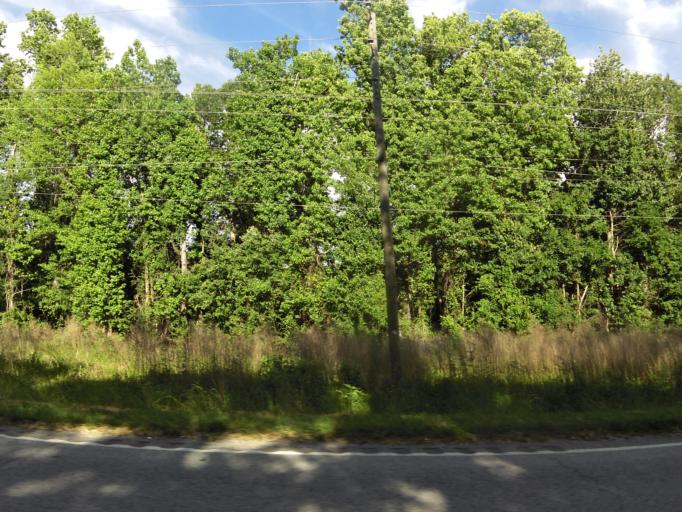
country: US
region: South Carolina
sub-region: Allendale County
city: Fairfax
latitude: 32.9335
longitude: -81.2371
